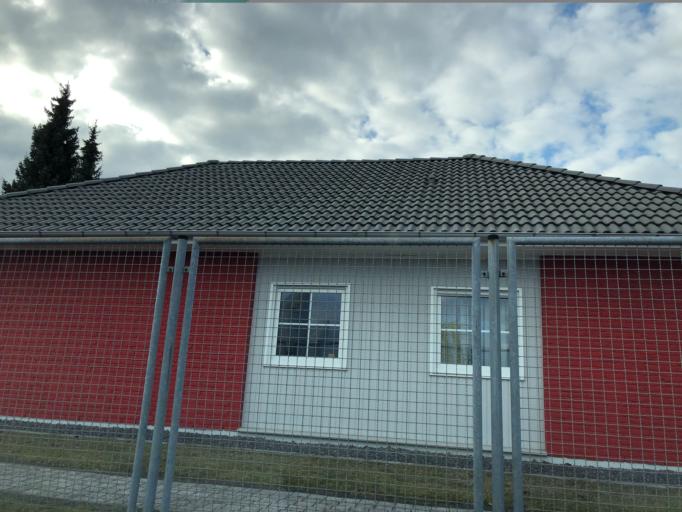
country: DE
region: Rheinland-Pfalz
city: Urmitz
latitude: 50.3954
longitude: 7.5246
